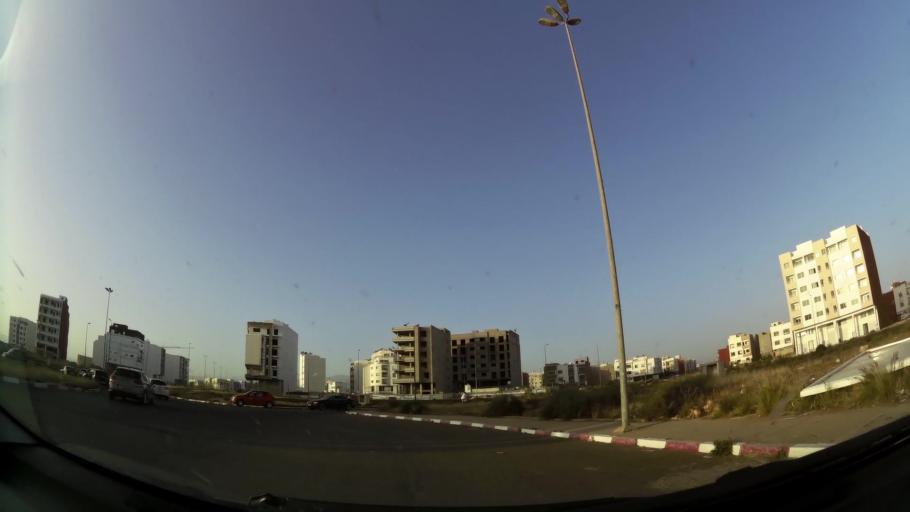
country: MA
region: Oued ed Dahab-Lagouira
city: Dakhla
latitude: 30.3994
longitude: -9.5775
